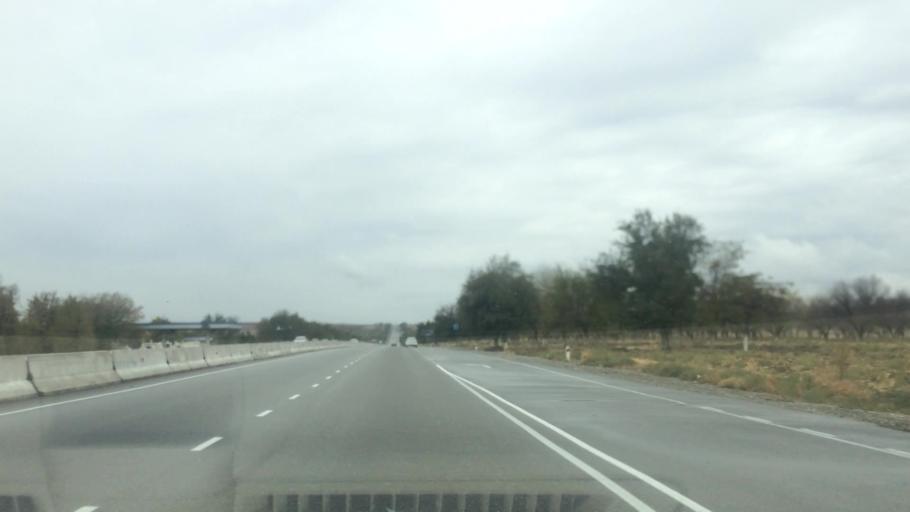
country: UZ
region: Samarqand
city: Bulung'ur
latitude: 39.8815
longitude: 67.4862
